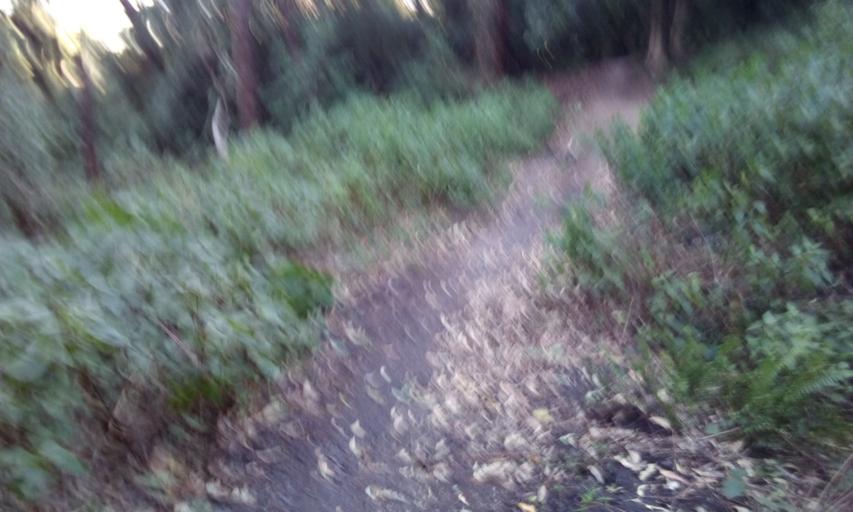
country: AU
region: New South Wales
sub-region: Wollongong
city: Keiraville
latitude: -34.4082
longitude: 150.8611
